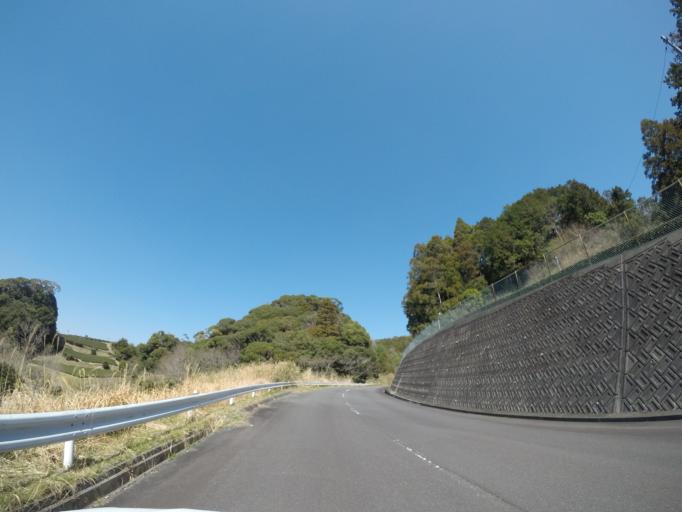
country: JP
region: Shizuoka
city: Kanaya
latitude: 34.7880
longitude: 138.1112
